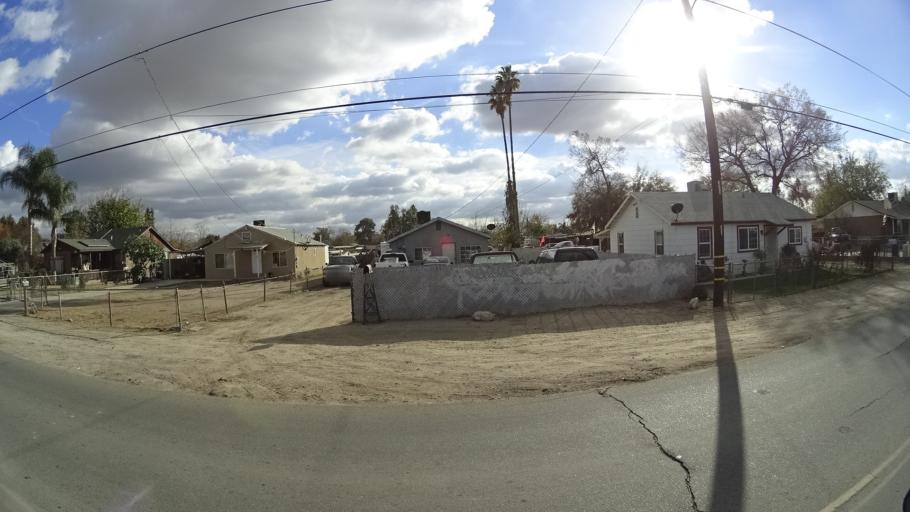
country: US
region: California
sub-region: Kern County
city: Greenfield
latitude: 35.3104
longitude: -118.9972
